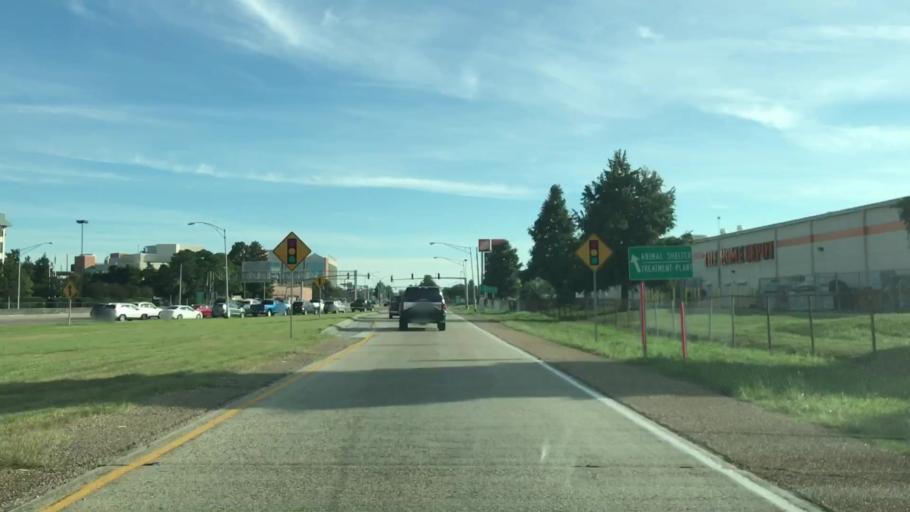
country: US
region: Louisiana
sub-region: Jefferson Parish
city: Elmwood
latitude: 29.9663
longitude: -90.1861
